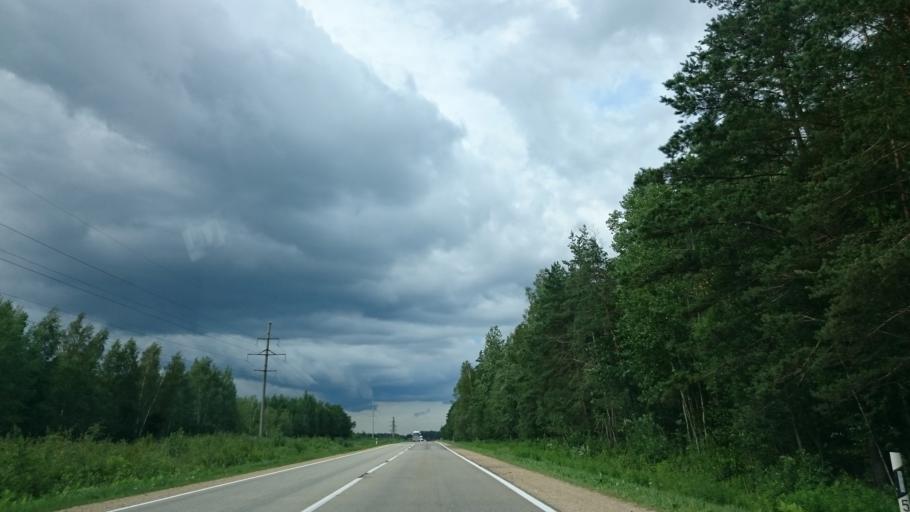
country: LV
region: Salaspils
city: Salaspils
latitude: 56.8720
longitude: 24.4072
